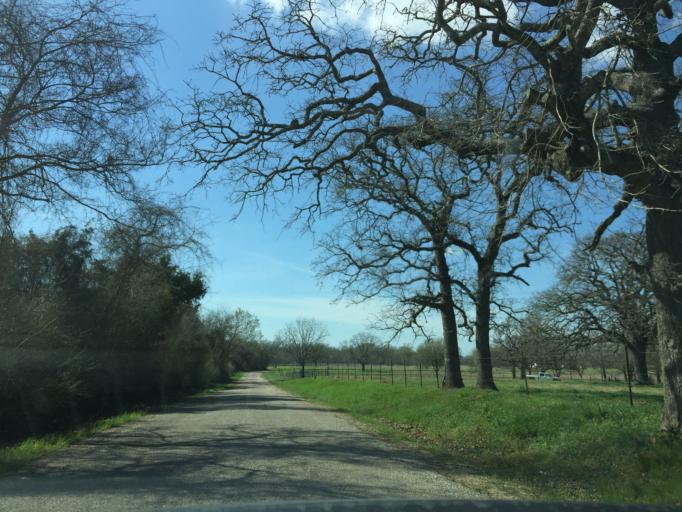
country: US
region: Texas
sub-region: Milam County
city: Thorndale
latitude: 30.5625
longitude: -97.1504
